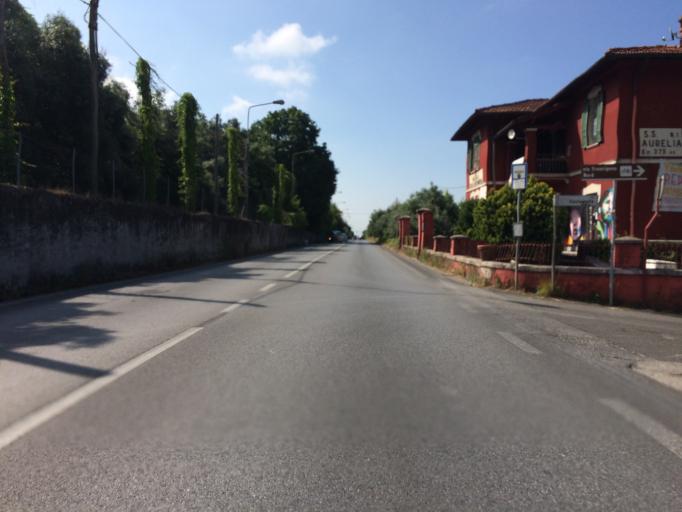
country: IT
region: Tuscany
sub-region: Provincia di Massa-Carrara
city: Capanne-Prato-Cinquale
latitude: 44.0129
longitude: 10.1578
